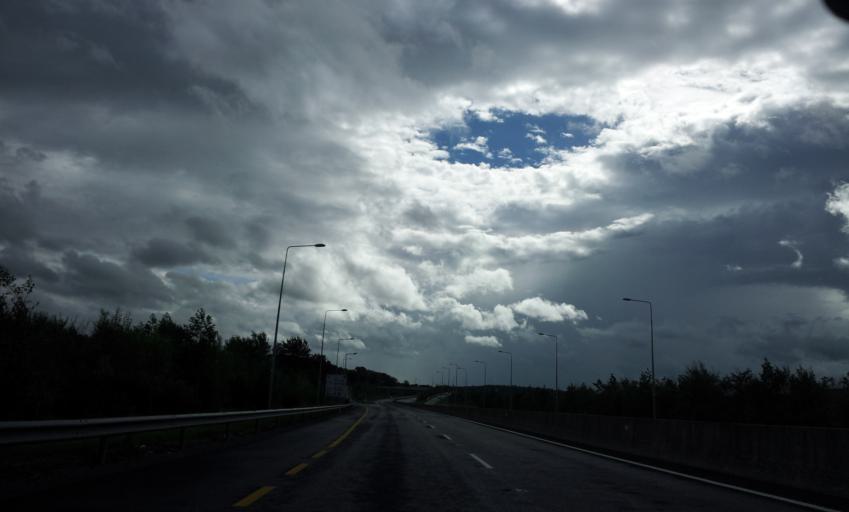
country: IE
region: Munster
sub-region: Waterford
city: Waterford
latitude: 52.2639
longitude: -7.1773
